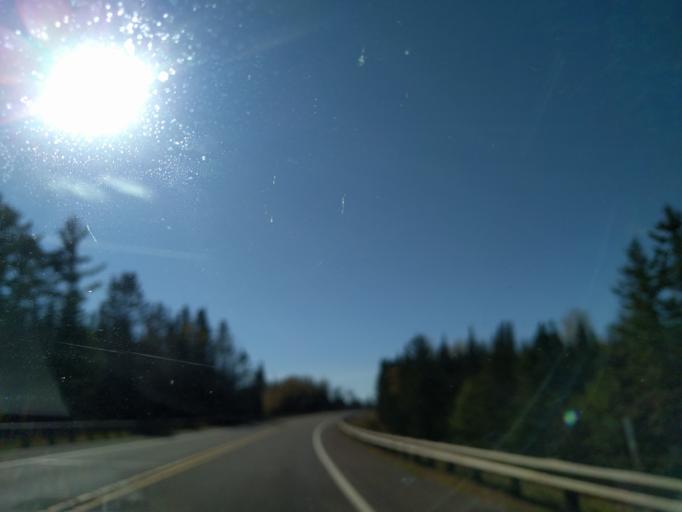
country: US
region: Michigan
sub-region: Marquette County
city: West Ishpeming
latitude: 46.4302
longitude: -87.9675
